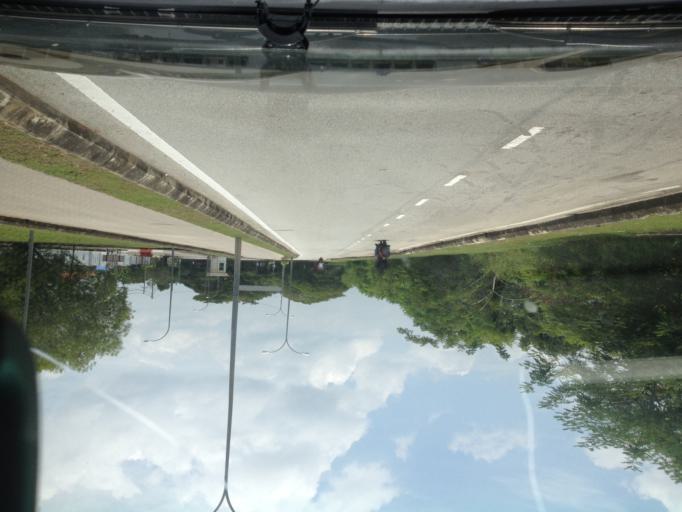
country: MY
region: Kedah
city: Sungai Petani
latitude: 5.6049
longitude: 100.5439
